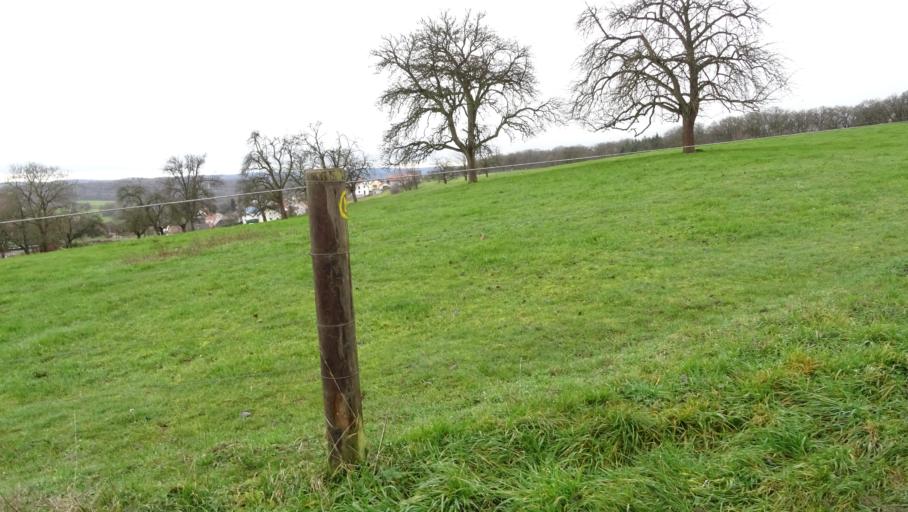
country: DE
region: Baden-Wuerttemberg
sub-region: Karlsruhe Region
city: Huffenhardt
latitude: 49.3208
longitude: 9.0672
